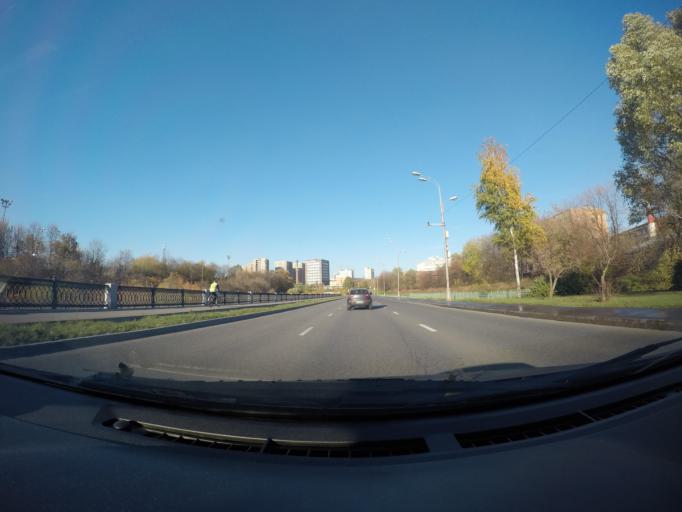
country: RU
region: Moskovskaya
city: Bogorodskoye
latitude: 55.8035
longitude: 37.7009
